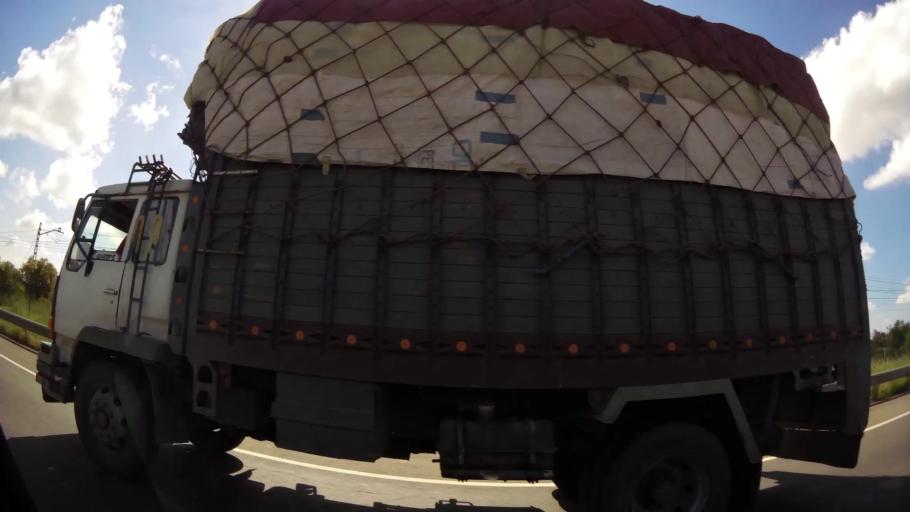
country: MA
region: Chaouia-Ouardigha
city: Nouaseur
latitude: 33.4160
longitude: -7.6267
